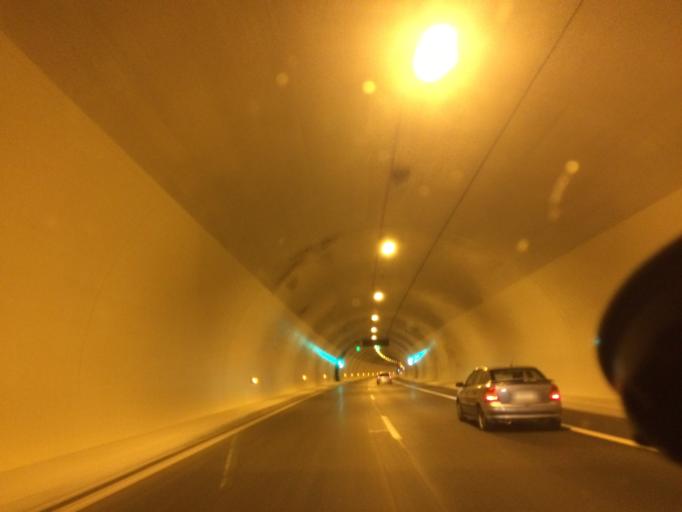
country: GR
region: Thessaly
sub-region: Nomos Larisis
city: Gonnoi
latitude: 39.8618
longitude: 22.5399
